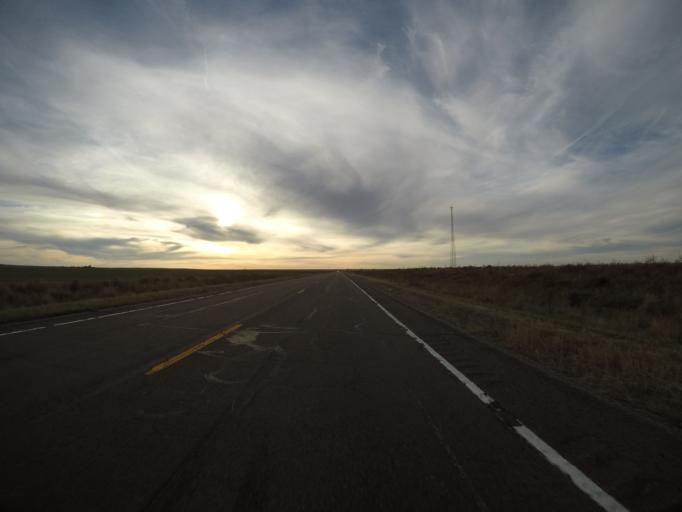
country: US
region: Colorado
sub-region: Yuma County
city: Yuma
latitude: 39.6700
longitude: -102.9396
